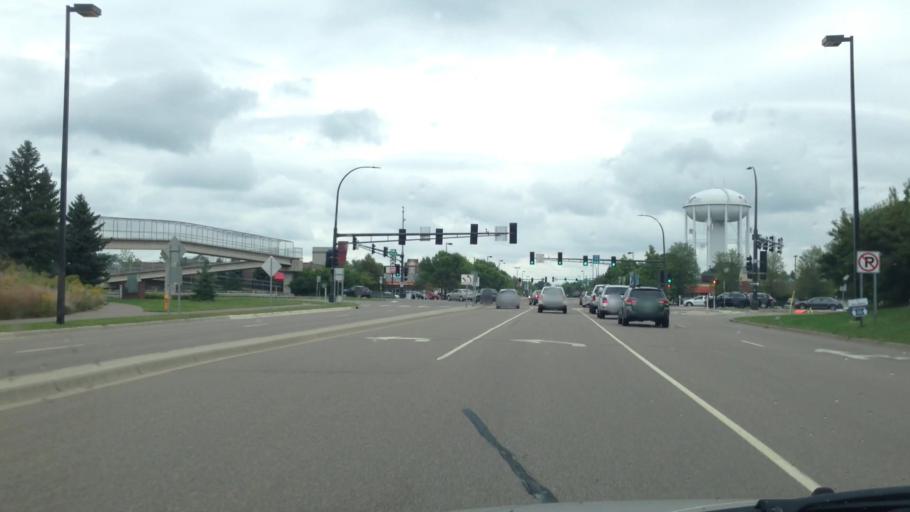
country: US
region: Minnesota
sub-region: Hennepin County
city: Golden Valley
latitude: 44.9827
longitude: -93.3803
